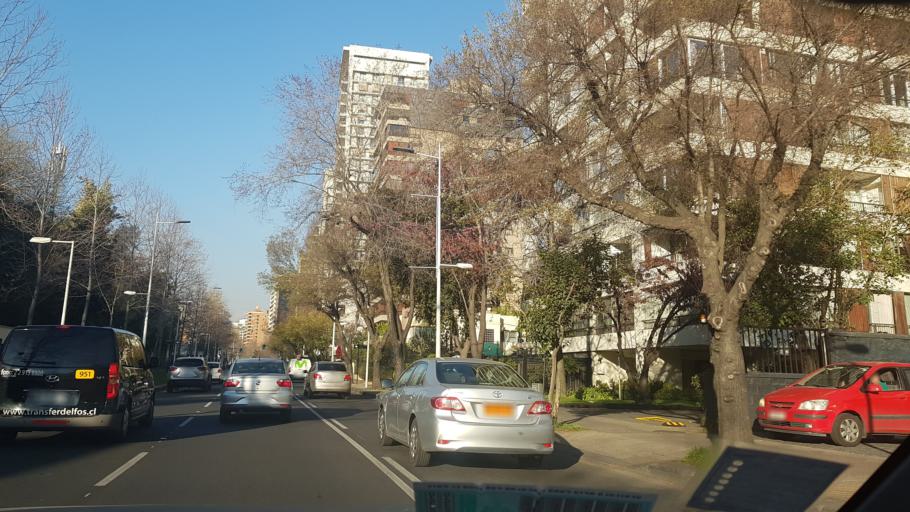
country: CL
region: Santiago Metropolitan
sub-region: Provincia de Santiago
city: Villa Presidente Frei, Nunoa, Santiago, Chile
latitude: -33.4125
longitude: -70.5948
